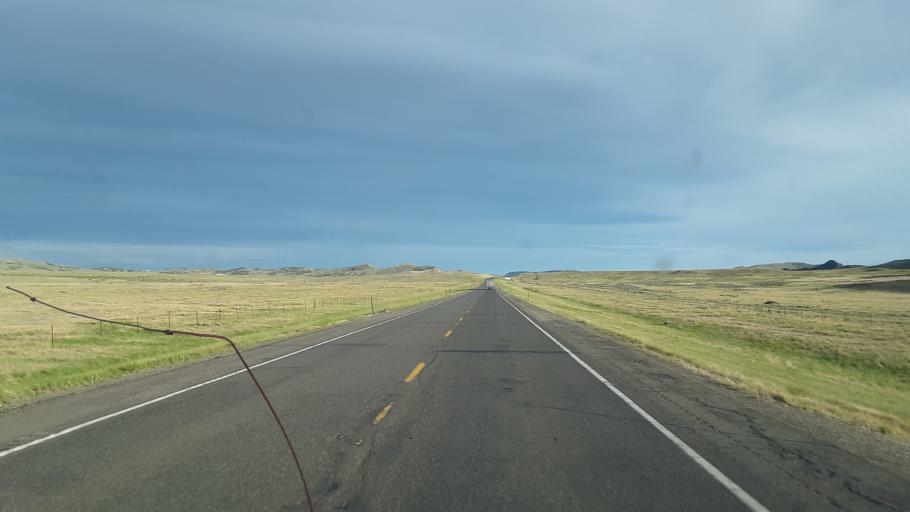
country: US
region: Wyoming
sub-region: Park County
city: Cody
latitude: 44.4734
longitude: -109.0195
